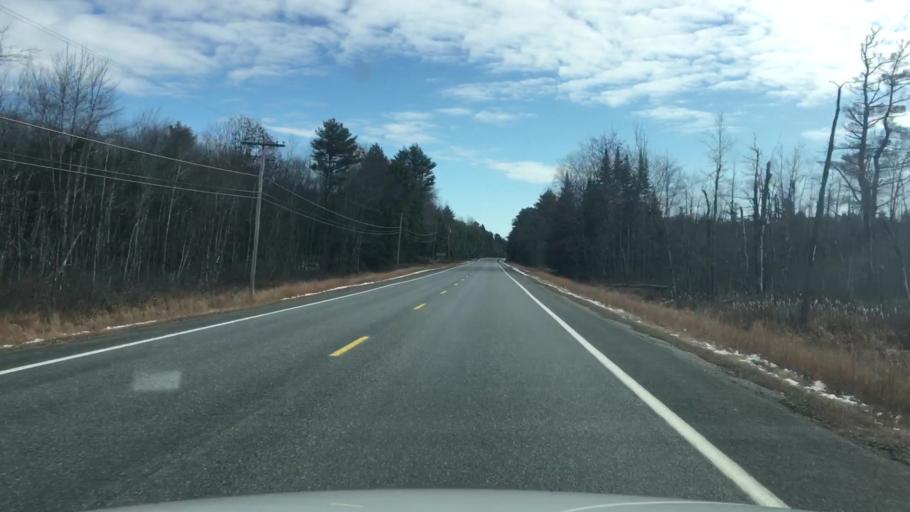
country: US
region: Maine
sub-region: Kennebec County
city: Wayne
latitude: 44.3480
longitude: -70.0452
